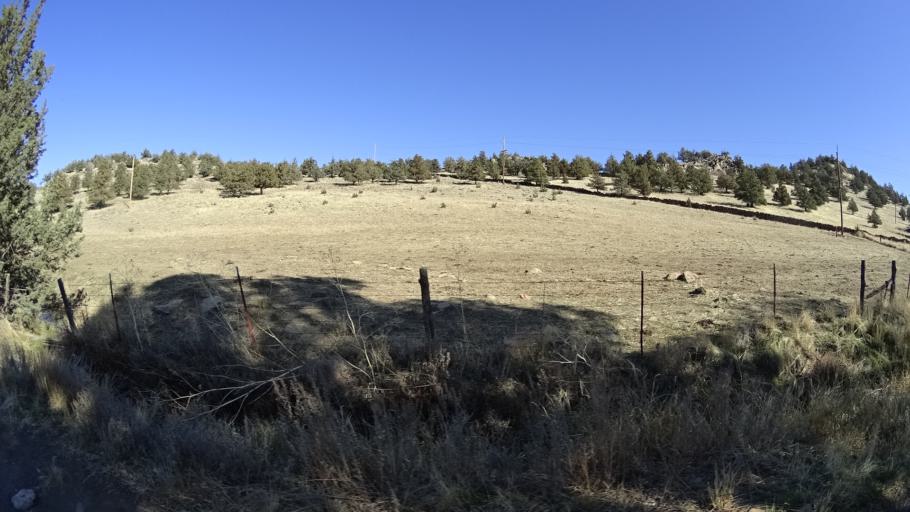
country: US
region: California
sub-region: Siskiyou County
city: Montague
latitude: 41.6897
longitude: -122.3709
